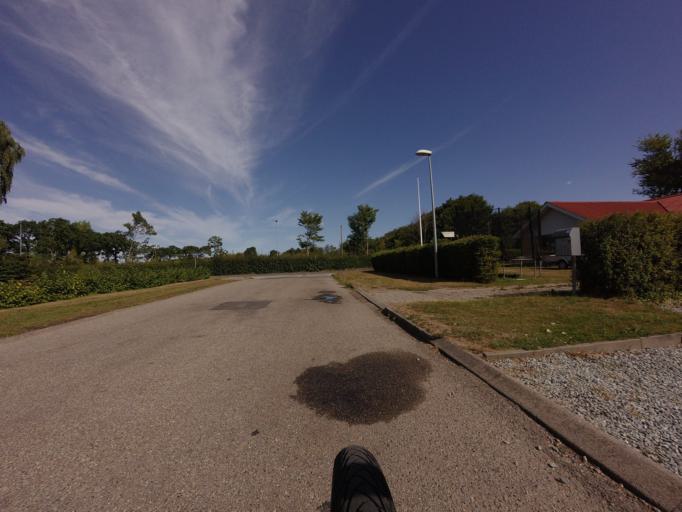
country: DK
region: North Denmark
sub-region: Hjorring Kommune
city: Vra
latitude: 57.4047
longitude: 9.9376
